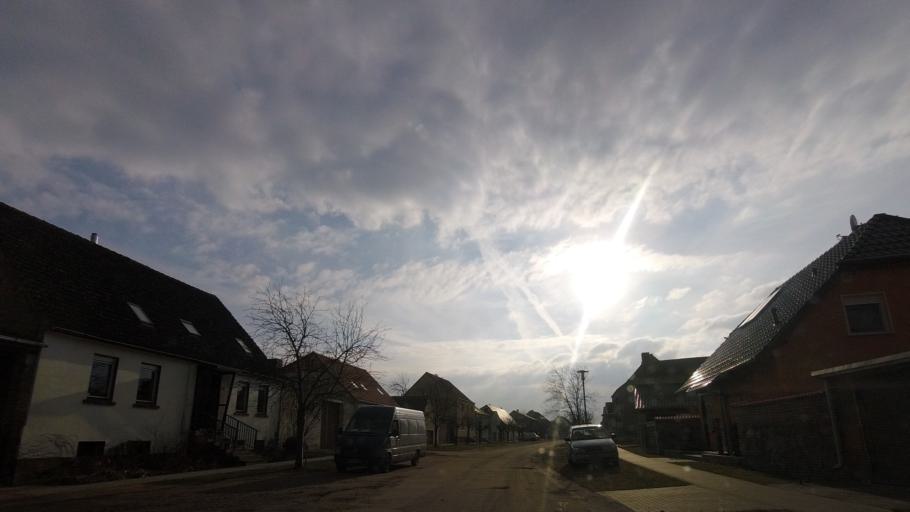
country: DE
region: Brandenburg
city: Belzig
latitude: 52.1929
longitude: 12.6431
